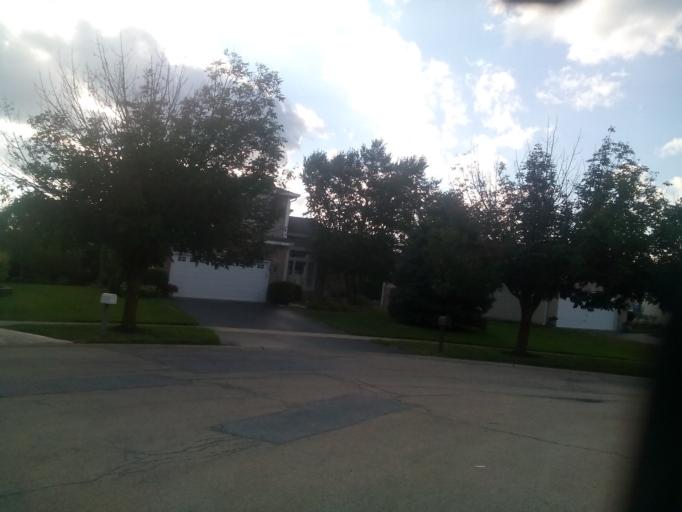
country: US
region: Illinois
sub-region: Will County
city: Plainfield
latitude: 41.6902
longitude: -88.1578
